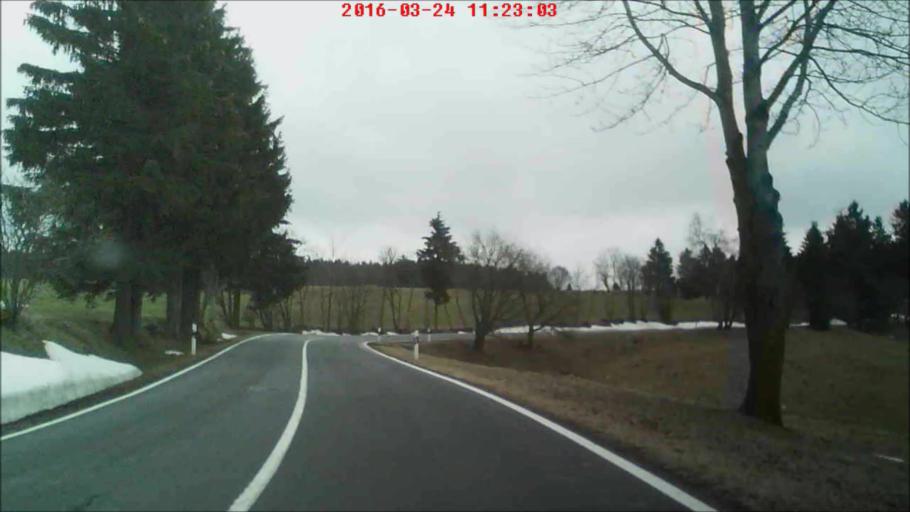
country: DE
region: Thuringia
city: Eisfeld
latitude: 50.4817
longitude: 10.9180
